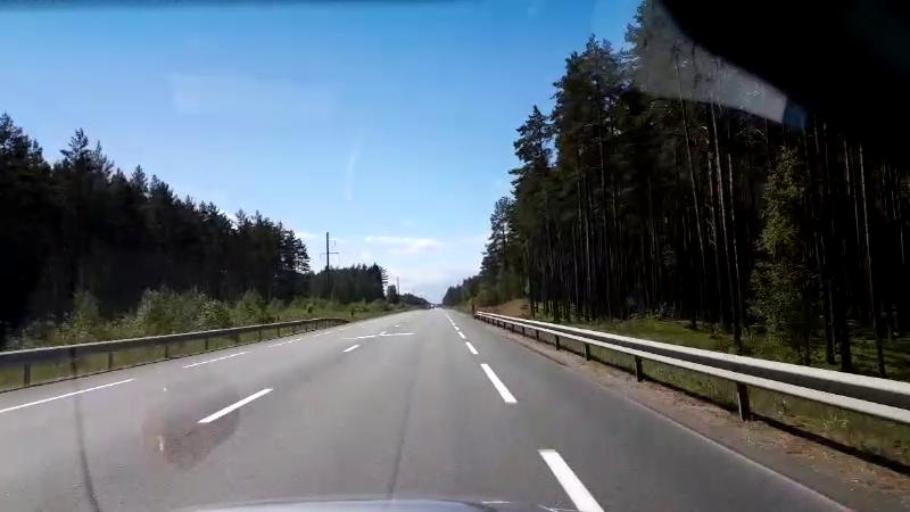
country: LV
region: Saulkrastu
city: Saulkrasti
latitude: 57.2228
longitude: 24.4117
